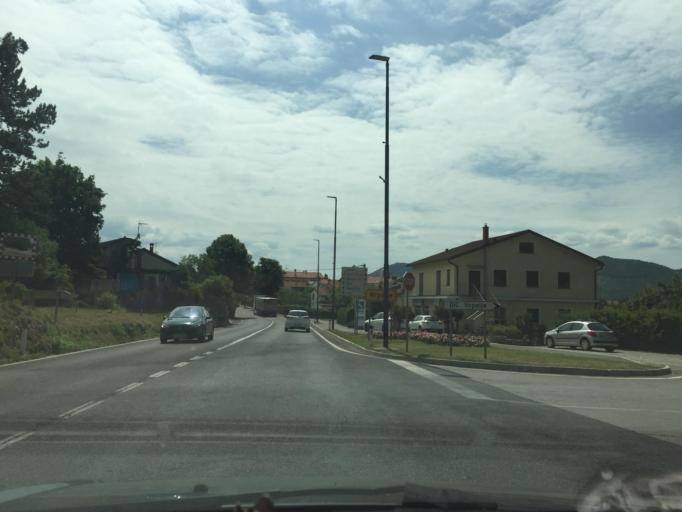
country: SI
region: Hrpelje-Kozina
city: Kozina
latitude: 45.6083
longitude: 13.9409
